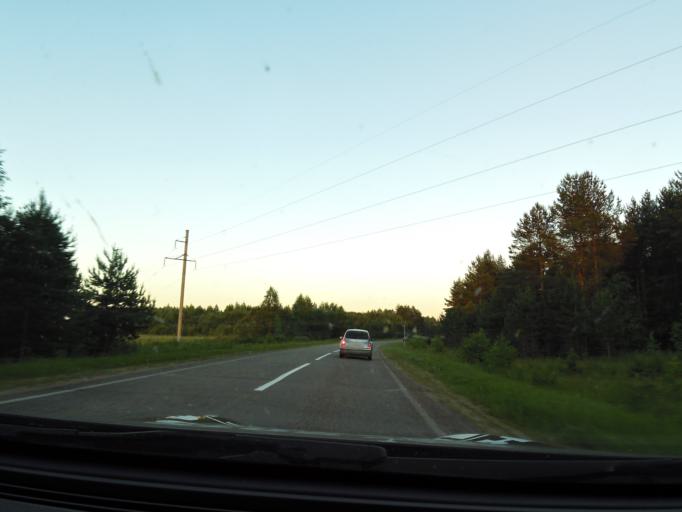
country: RU
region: Jaroslavl
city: Lyubim
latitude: 58.3485
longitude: 40.8188
